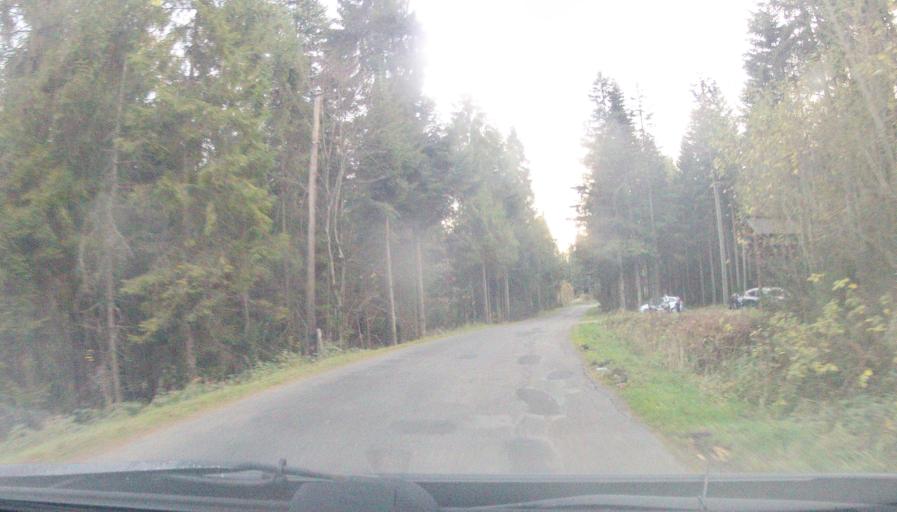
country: PL
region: Lesser Poland Voivodeship
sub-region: Powiat suski
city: Krzeszow
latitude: 49.7596
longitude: 19.4588
